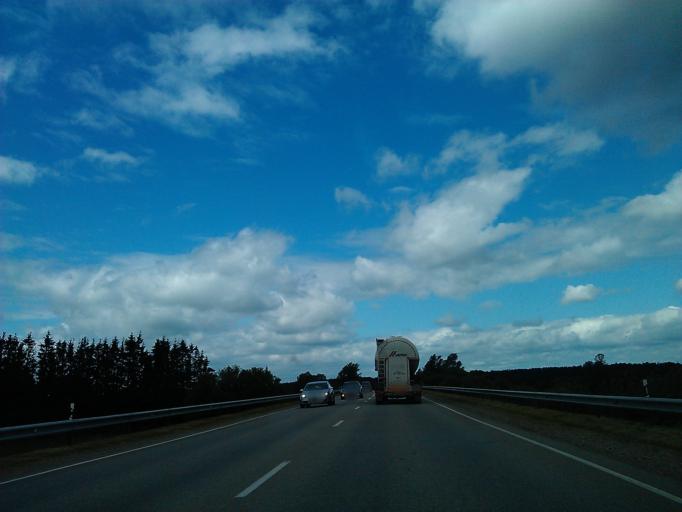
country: LV
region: Tukuma Rajons
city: Tukums
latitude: 56.9386
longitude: 23.1745
